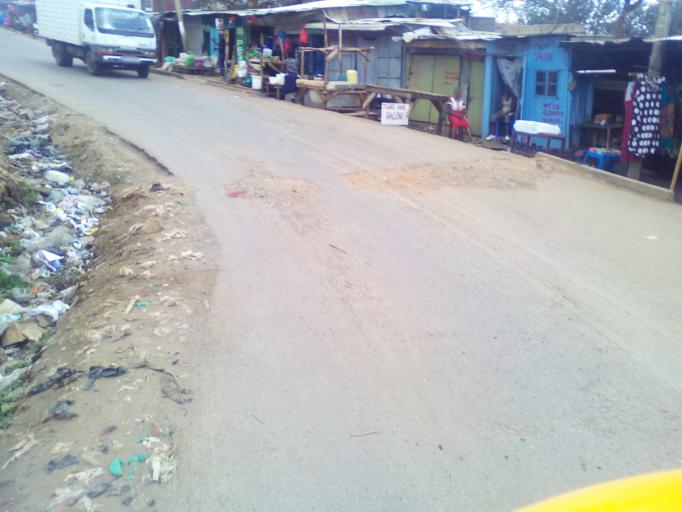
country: KE
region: Nairobi Area
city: Nairobi
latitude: -1.3159
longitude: 36.8018
